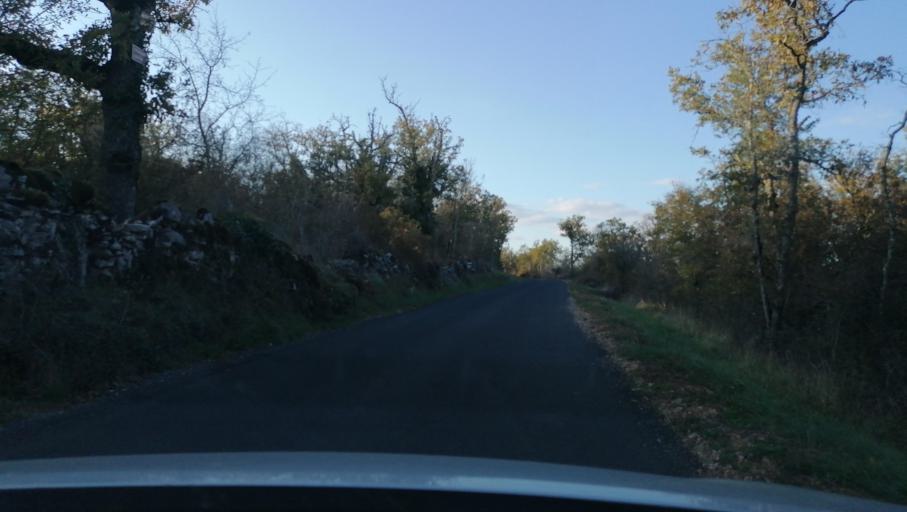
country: FR
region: Midi-Pyrenees
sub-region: Departement du Lot
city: Vayrac
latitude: 44.8685
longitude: 1.6649
